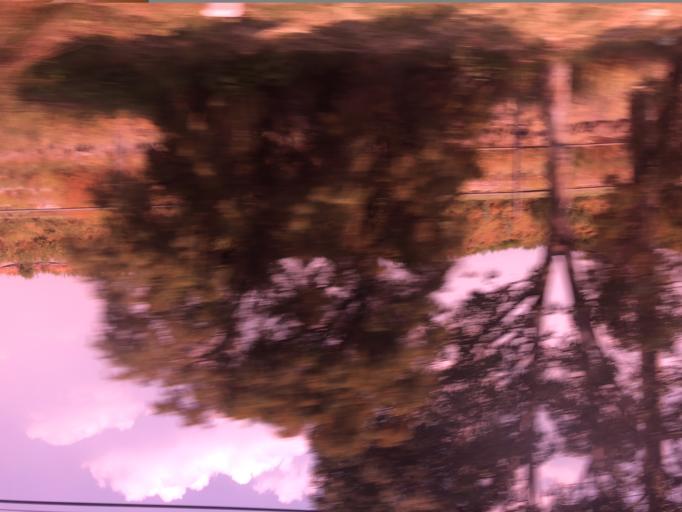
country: MX
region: Mexico
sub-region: Ciudad Nezahualcoyotl
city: Colonia Gustavo Baz Prada
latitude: 19.4649
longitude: -99.0172
